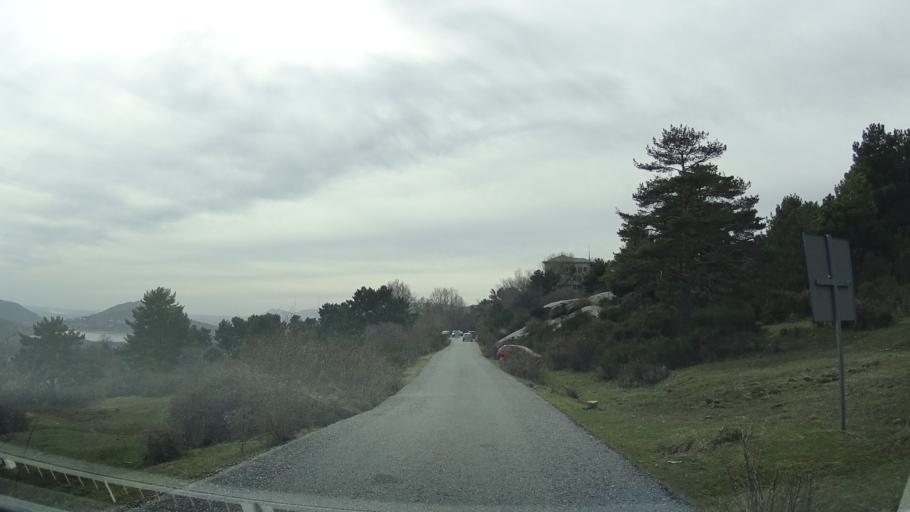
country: ES
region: Madrid
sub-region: Provincia de Madrid
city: Navacerrada
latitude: 40.7457
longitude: -3.9974
